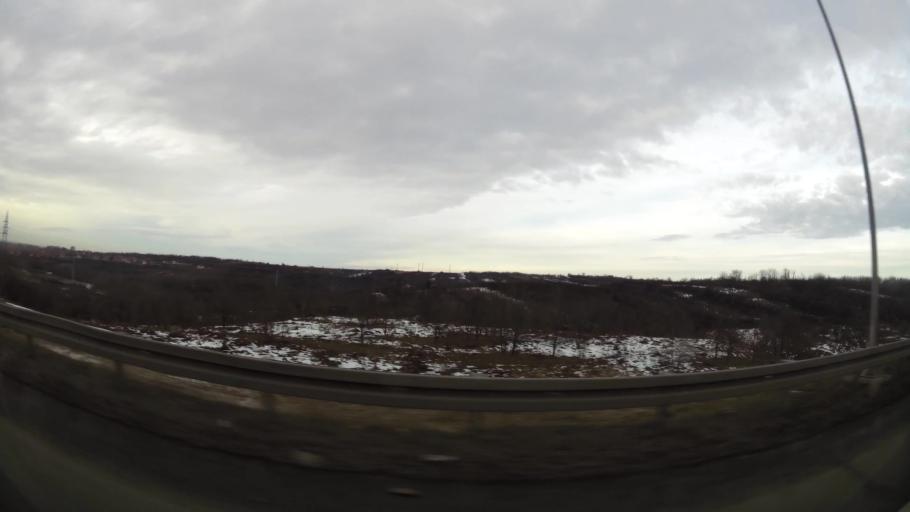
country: RS
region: Central Serbia
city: Sremcica
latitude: 44.7146
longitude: 20.4081
